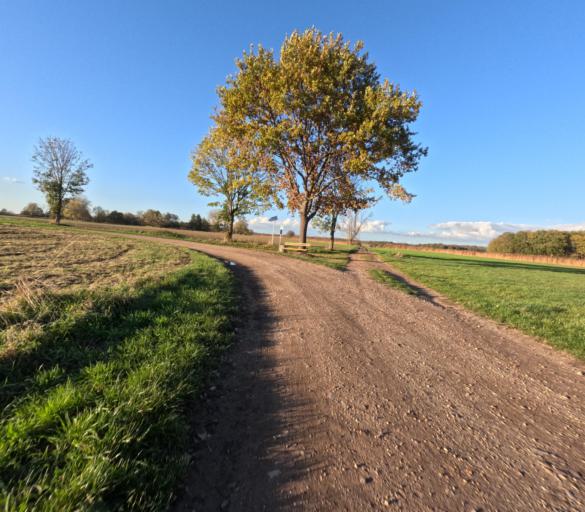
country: DE
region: Saxony-Anhalt
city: Zoschen
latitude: 51.3645
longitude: 12.1304
